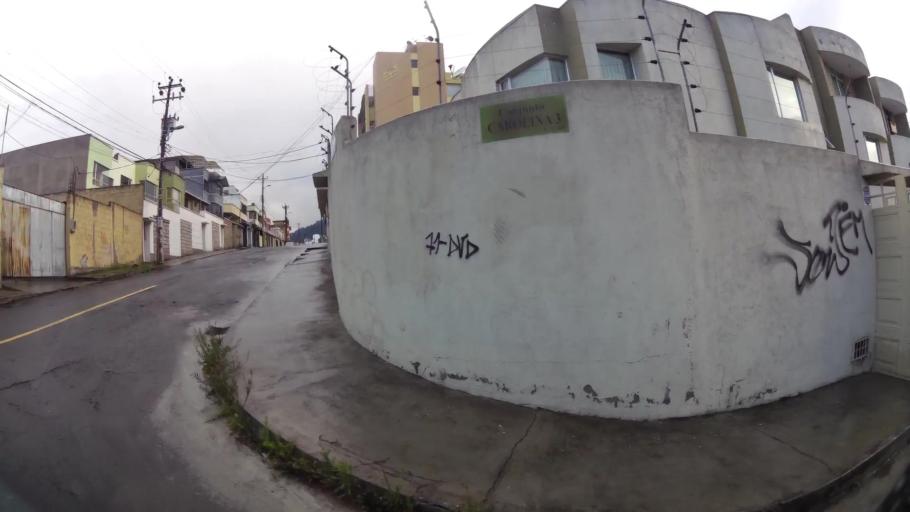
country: EC
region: Pichincha
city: Quito
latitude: -0.1056
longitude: -78.4873
